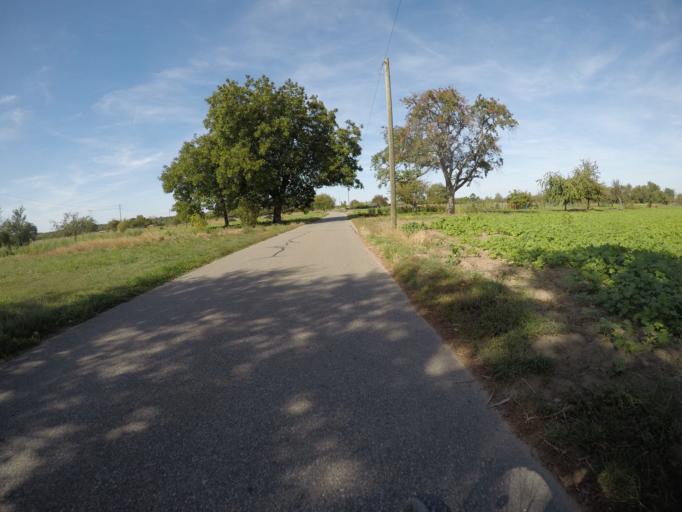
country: DE
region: Baden-Wuerttemberg
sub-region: Karlsruhe Region
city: Ubstadt-Weiher
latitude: 49.1845
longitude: 8.6198
